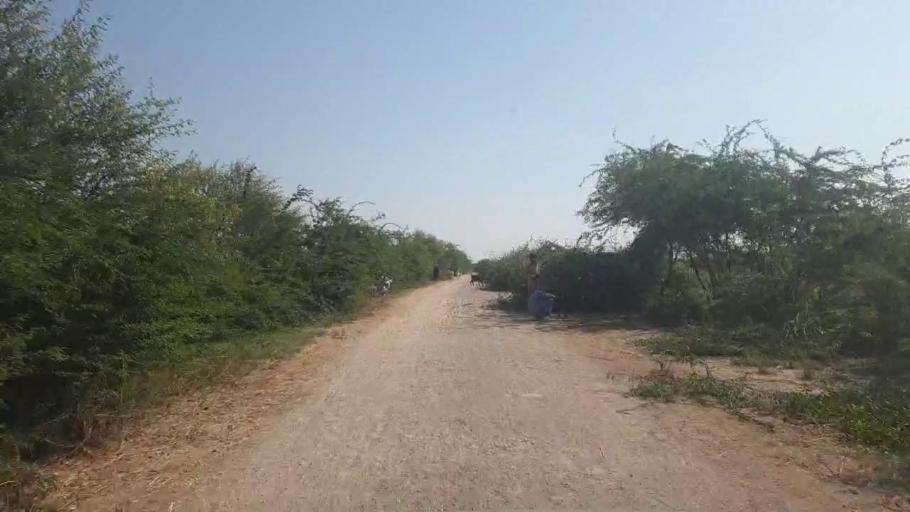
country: PK
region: Sindh
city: Badin
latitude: 24.5825
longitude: 68.8456
